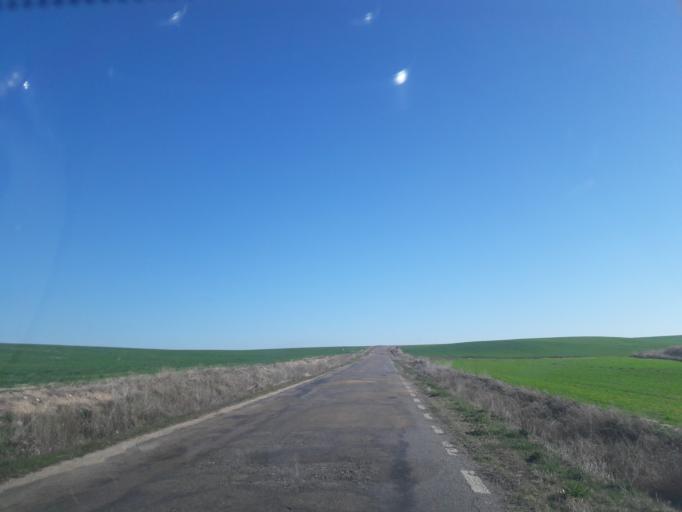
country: ES
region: Castille and Leon
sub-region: Provincia de Salamanca
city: Tordillos
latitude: 40.8666
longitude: -5.3361
